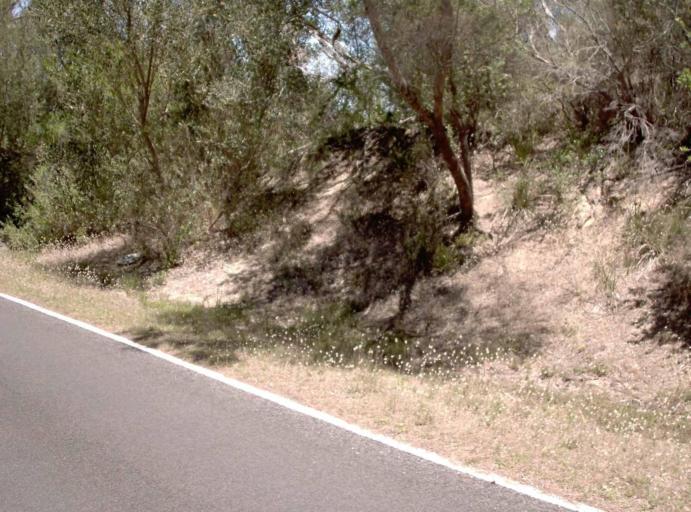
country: AU
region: Victoria
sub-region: Latrobe
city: Morwell
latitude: -38.8684
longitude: 146.2630
